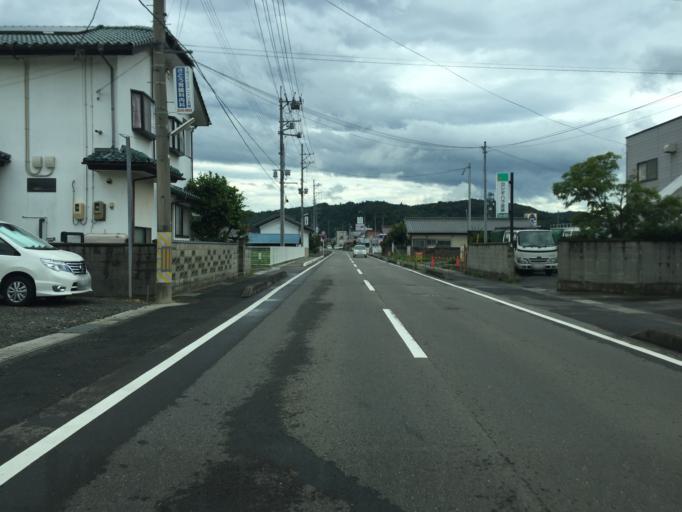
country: JP
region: Fukushima
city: Fukushima-shi
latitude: 37.7294
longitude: 140.4711
